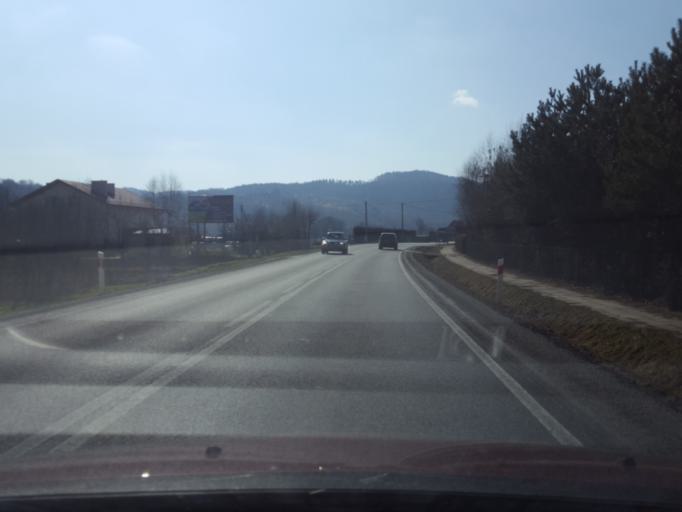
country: PL
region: Lesser Poland Voivodeship
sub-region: Powiat brzeski
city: Czchow
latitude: 49.8257
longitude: 20.6792
